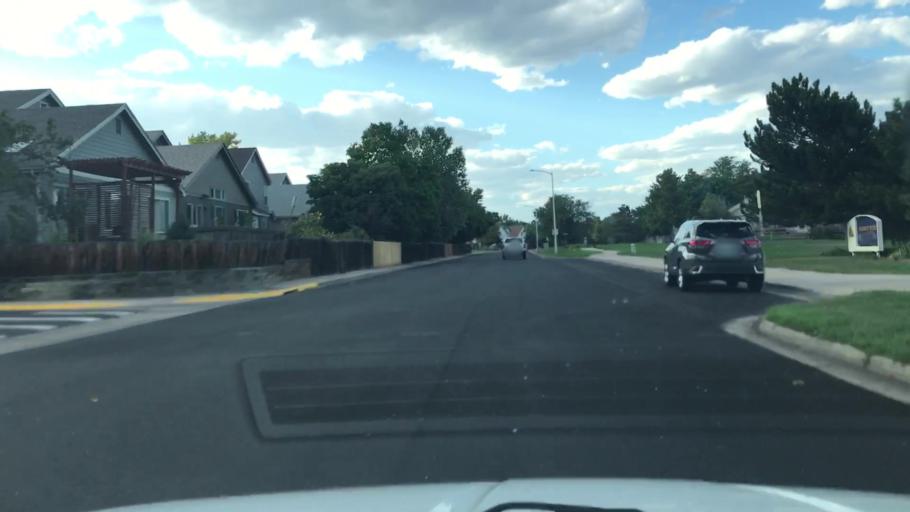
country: US
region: Colorado
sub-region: Broomfield County
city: Broomfield
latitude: 39.9240
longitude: -105.0396
